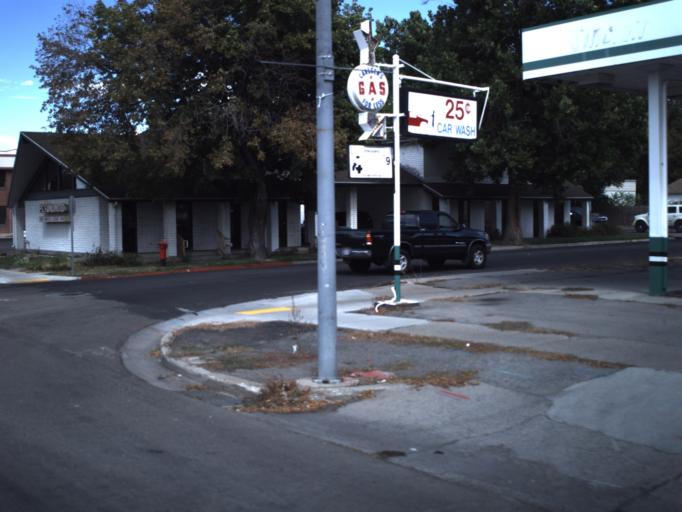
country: US
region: Utah
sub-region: Cache County
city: Logan
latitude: 41.7427
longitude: -111.8346
